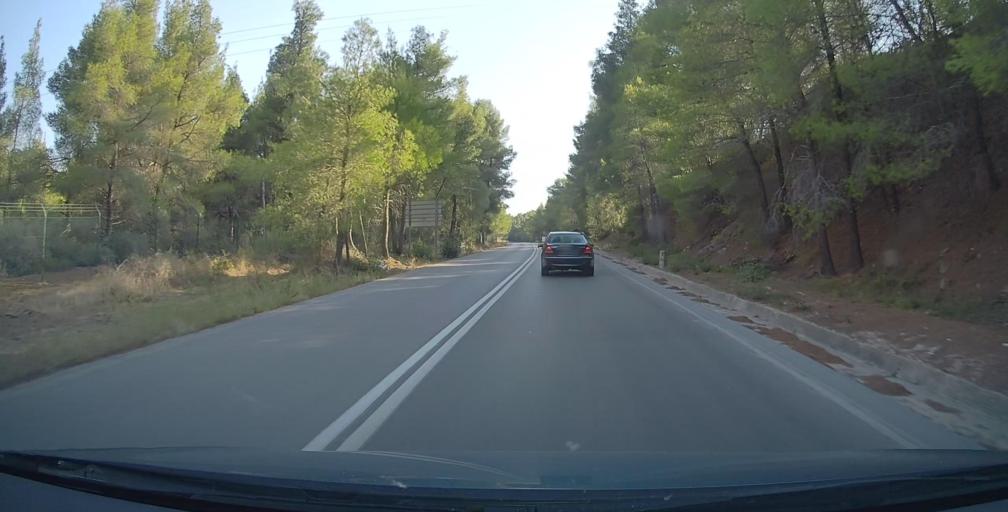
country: GR
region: Central Macedonia
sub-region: Nomos Chalkidikis
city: Neos Marmaras
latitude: 40.0708
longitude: 23.8052
